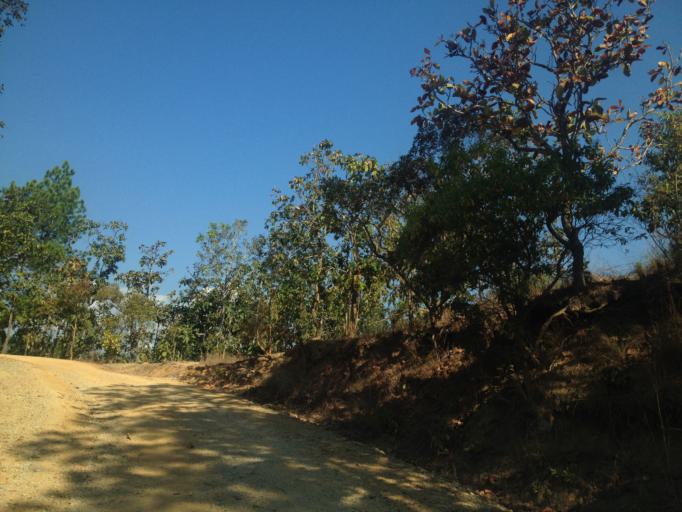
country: TH
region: Mae Hong Son
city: Ban Huai I Huak
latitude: 18.1218
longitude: 98.2039
